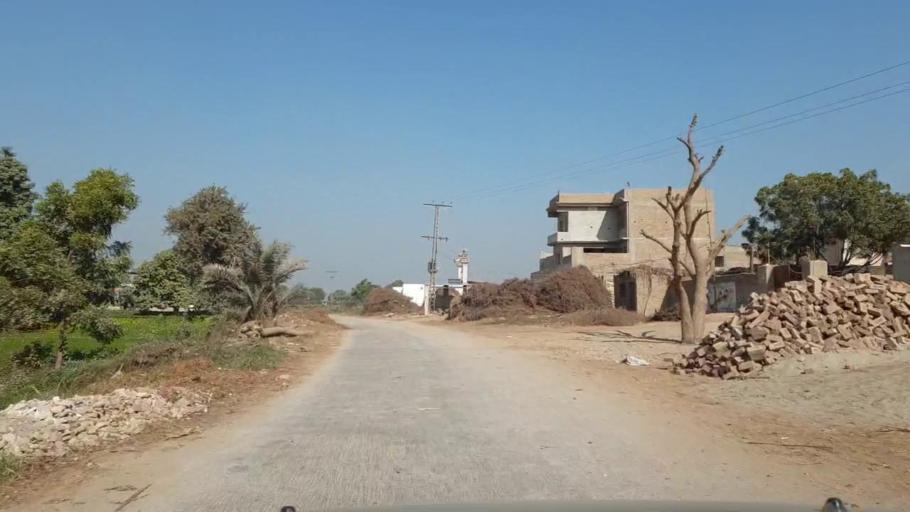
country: PK
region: Sindh
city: Matiari
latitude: 25.5982
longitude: 68.6010
